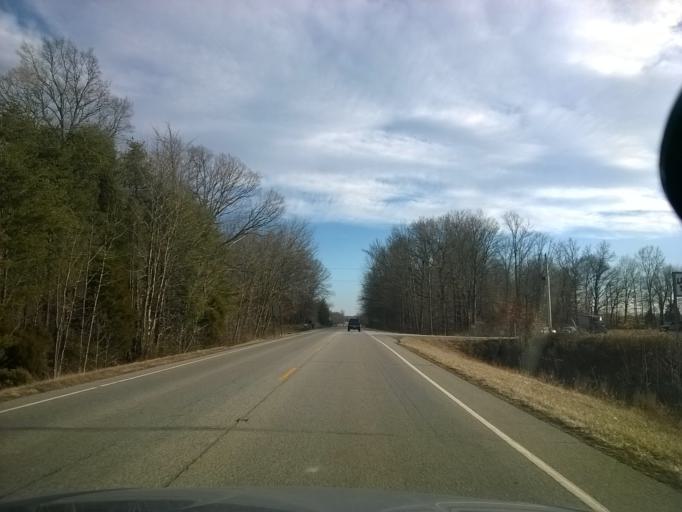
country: US
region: Indiana
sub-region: Scott County
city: Austin
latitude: 38.7775
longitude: -85.8274
